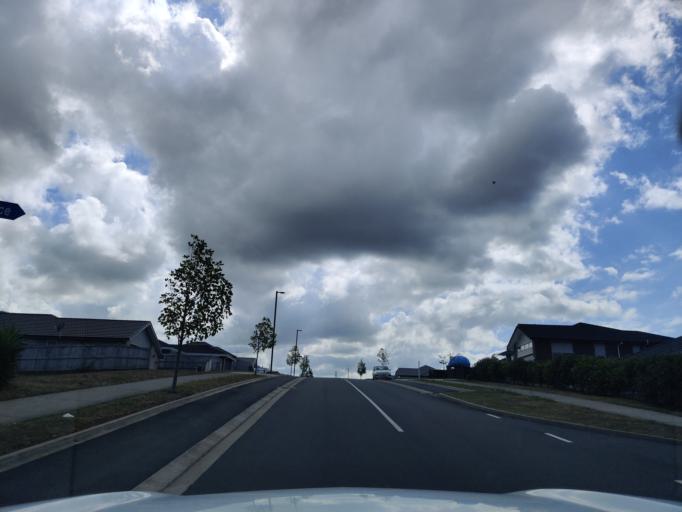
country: NZ
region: Auckland
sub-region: Auckland
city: Pukekohe East
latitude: -37.2338
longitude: 175.0115
